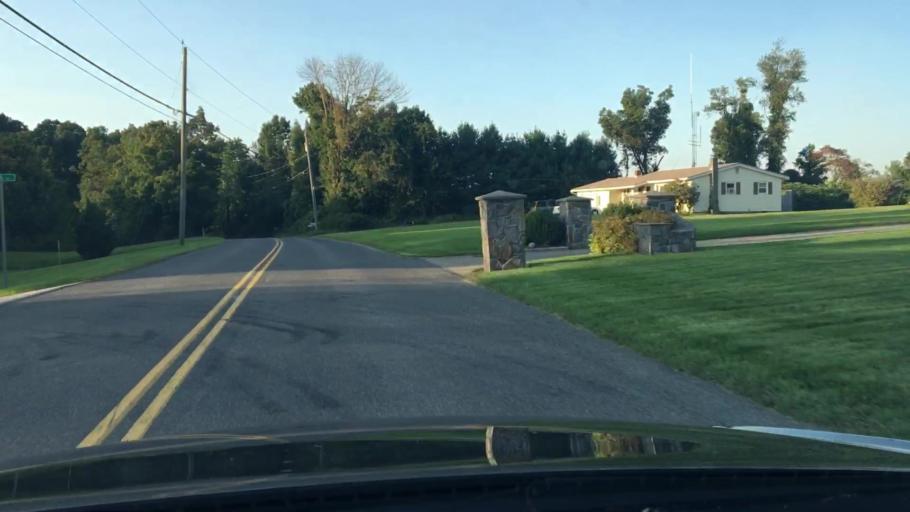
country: US
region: Connecticut
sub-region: Litchfield County
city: New Milford
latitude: 41.6127
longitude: -73.3723
